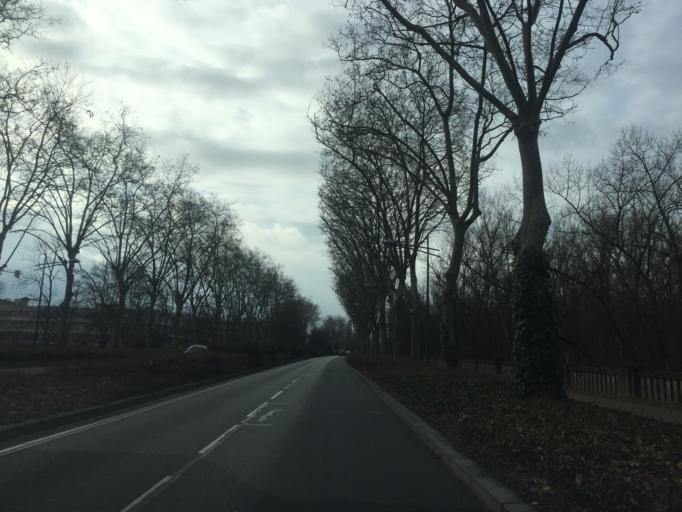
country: FR
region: Rhone-Alpes
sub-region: Departement du Rhone
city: Villeurbanne
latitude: 45.7857
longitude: 4.8721
